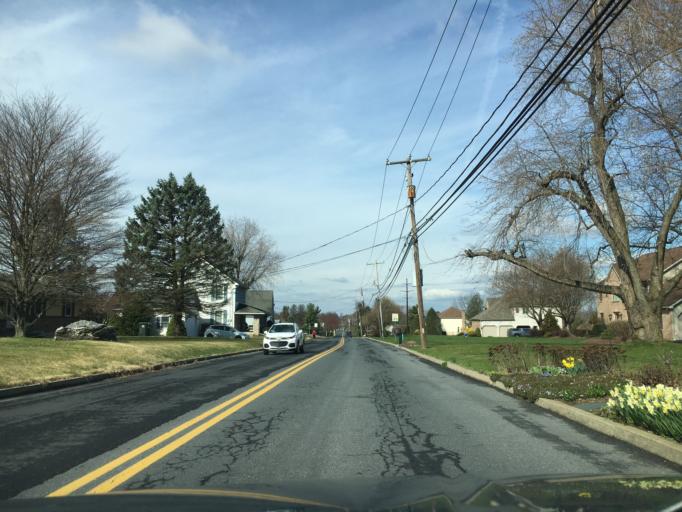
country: US
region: Pennsylvania
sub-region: Northampton County
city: Bath
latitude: 40.6833
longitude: -75.4214
